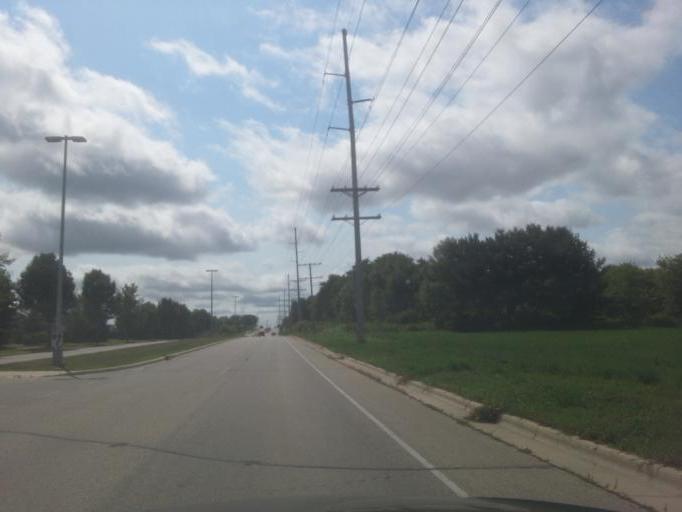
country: US
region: Wisconsin
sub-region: Dane County
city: Cottage Grove
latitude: 43.0960
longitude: -89.2669
